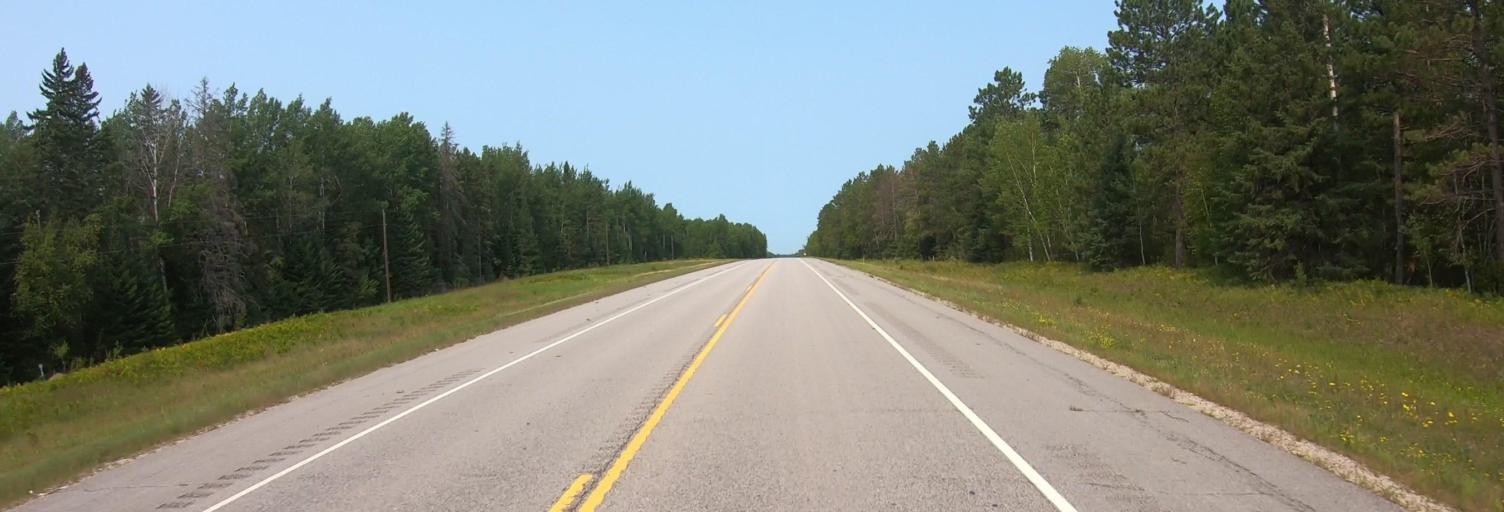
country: CA
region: Ontario
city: Fort Frances
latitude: 48.3767
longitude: -92.9814
